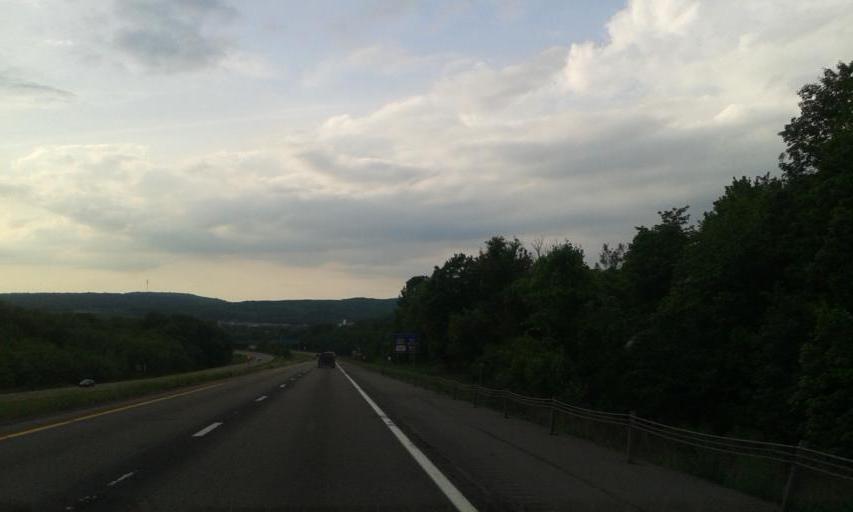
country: US
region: New York
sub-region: Broome County
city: Chenango Bridge
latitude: 42.0887
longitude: -75.8102
